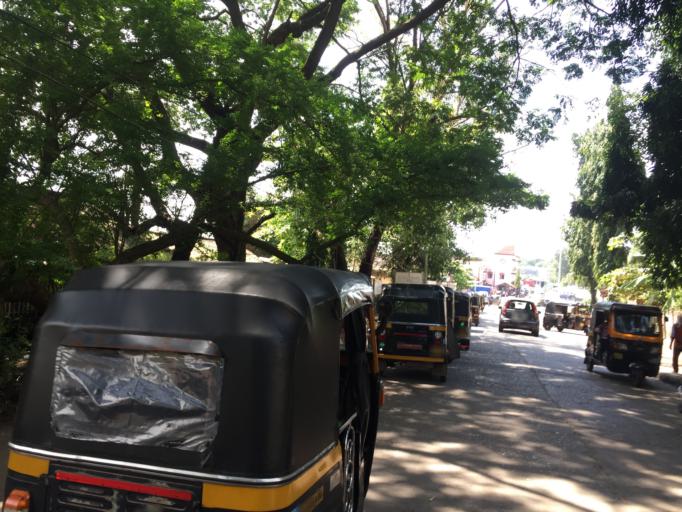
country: IN
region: Karnataka
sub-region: Dakshina Kannada
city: Mangalore
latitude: 12.8651
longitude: 74.8431
